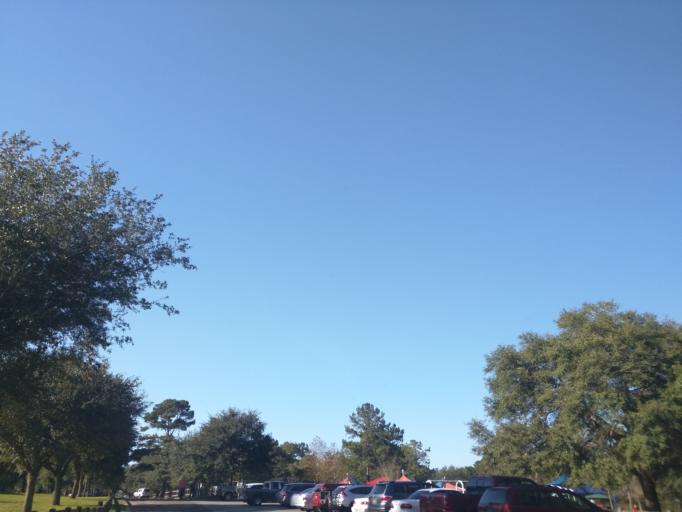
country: US
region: Florida
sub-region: Leon County
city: Tallahassee
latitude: 30.4462
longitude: -84.2117
